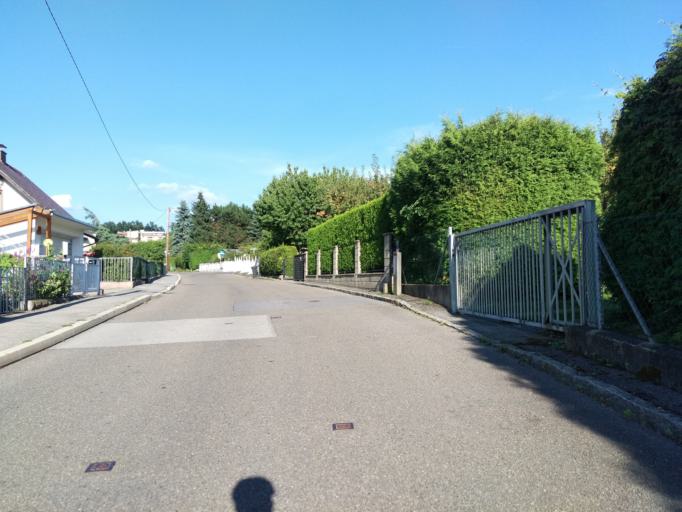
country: AT
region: Styria
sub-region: Graz Stadt
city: Graz
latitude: 47.0690
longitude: 15.4772
